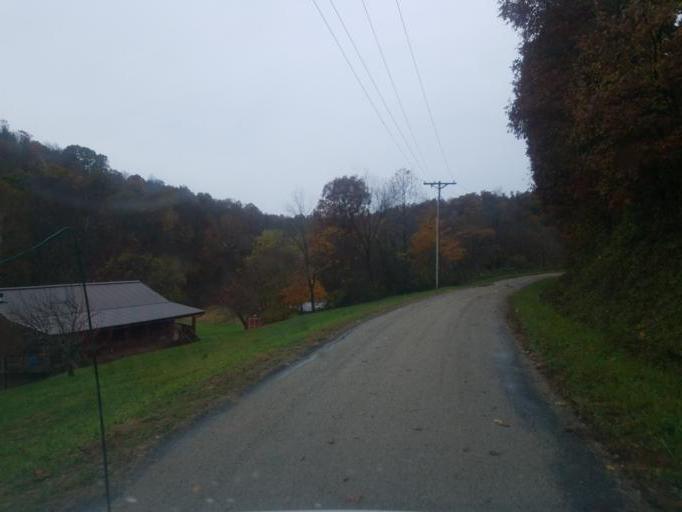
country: US
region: Ohio
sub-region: Washington County
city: Beverly
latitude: 39.4644
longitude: -81.7619
